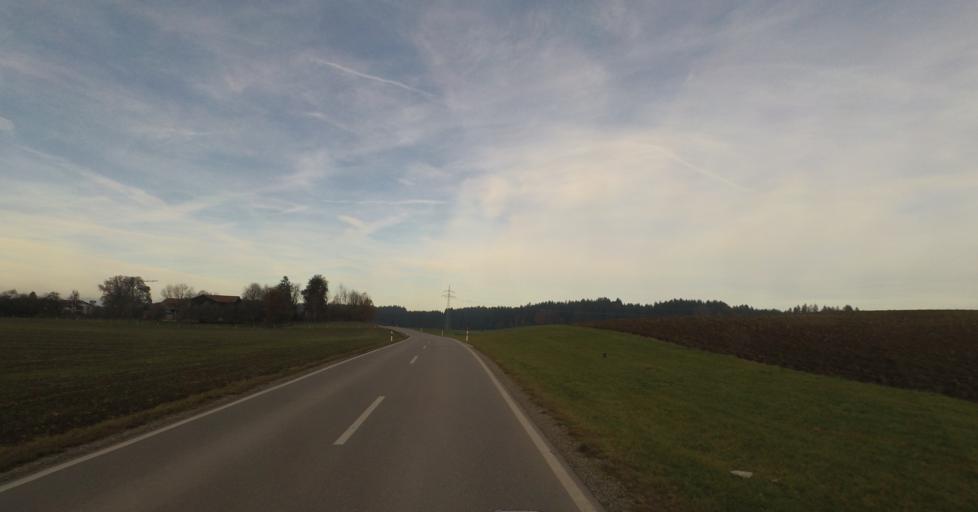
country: DE
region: Bavaria
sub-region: Upper Bavaria
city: Nussdorf
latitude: 47.8853
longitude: 12.6110
